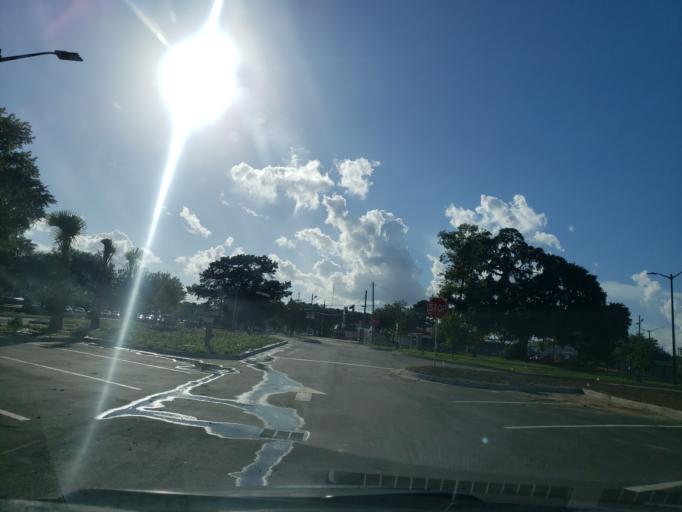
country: US
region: Georgia
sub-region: Chatham County
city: Montgomery
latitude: 31.9905
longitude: -81.1270
